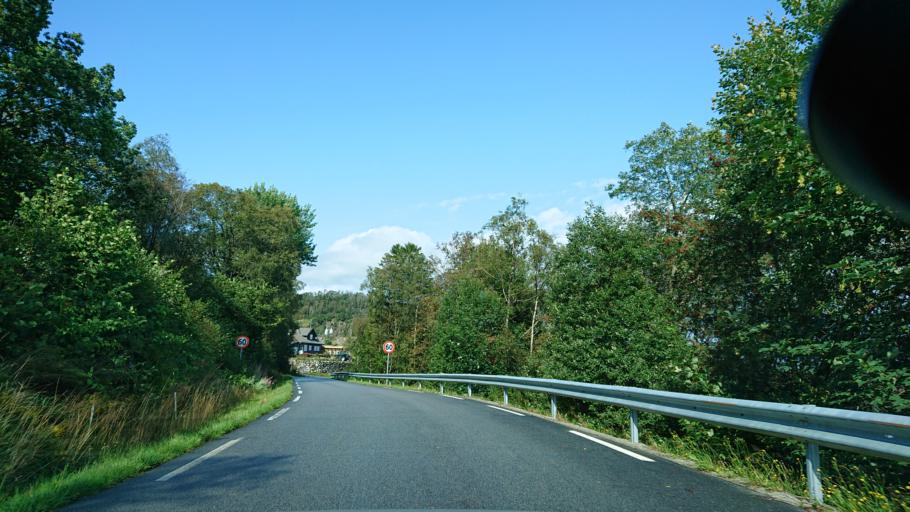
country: NO
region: Rogaland
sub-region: Gjesdal
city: Algard
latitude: 58.6919
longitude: 5.8803
